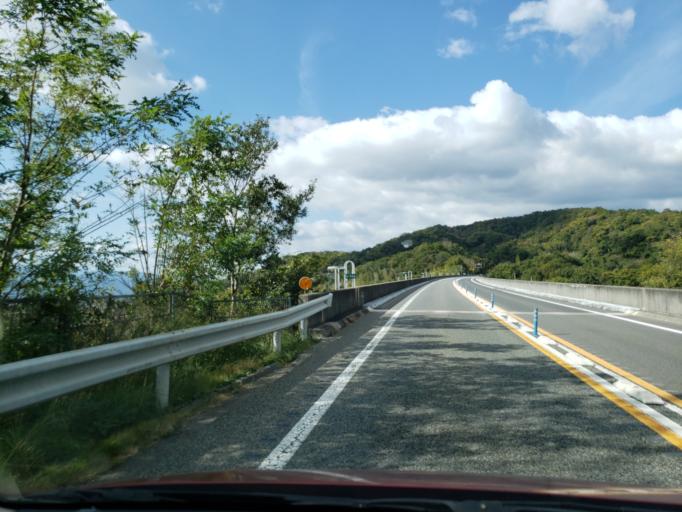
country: JP
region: Tokushima
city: Kamojimacho-jogejima
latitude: 34.1041
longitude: 134.3000
